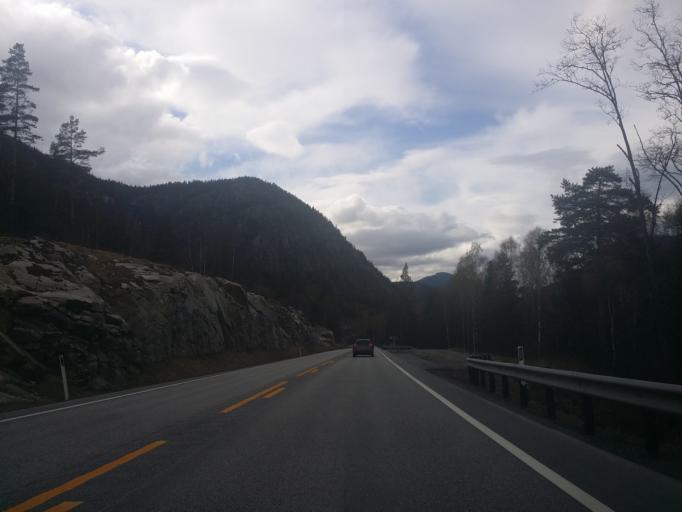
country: NO
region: Buskerud
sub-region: Fla
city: Fla
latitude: 60.4553
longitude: 9.2707
